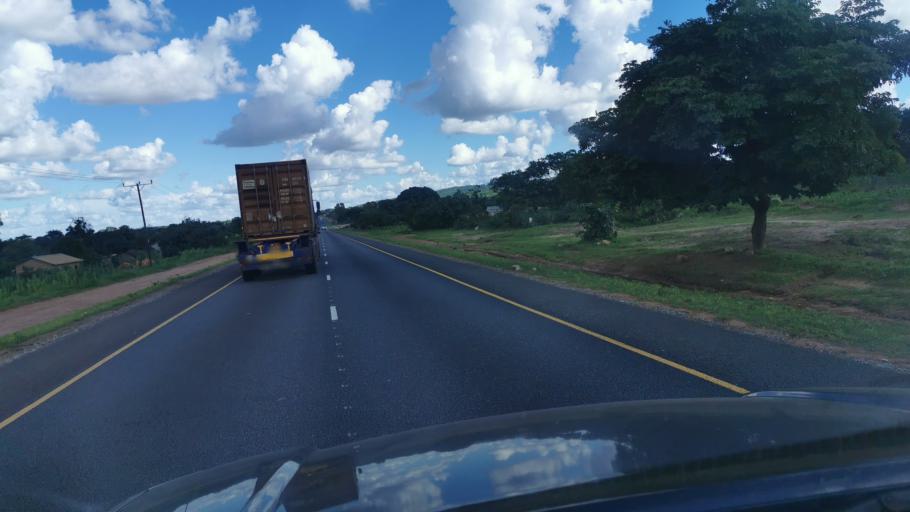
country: TZ
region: Geita
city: Ushirombo
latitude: -3.4377
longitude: 31.8364
